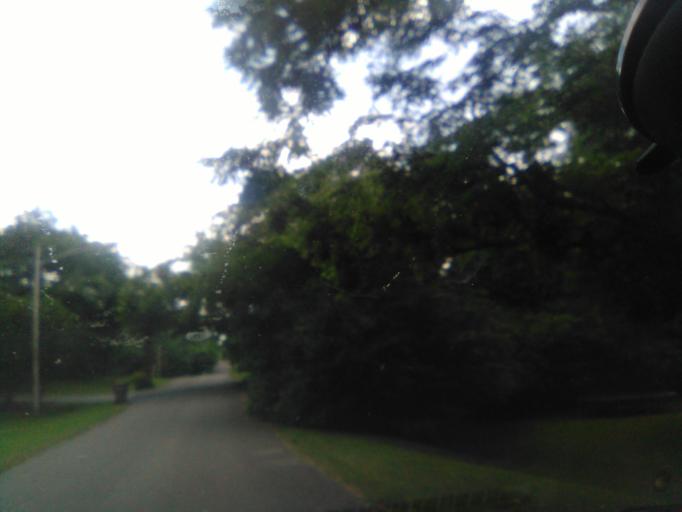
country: US
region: Tennessee
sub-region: Davidson County
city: Belle Meade
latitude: 36.1221
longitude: -86.8774
